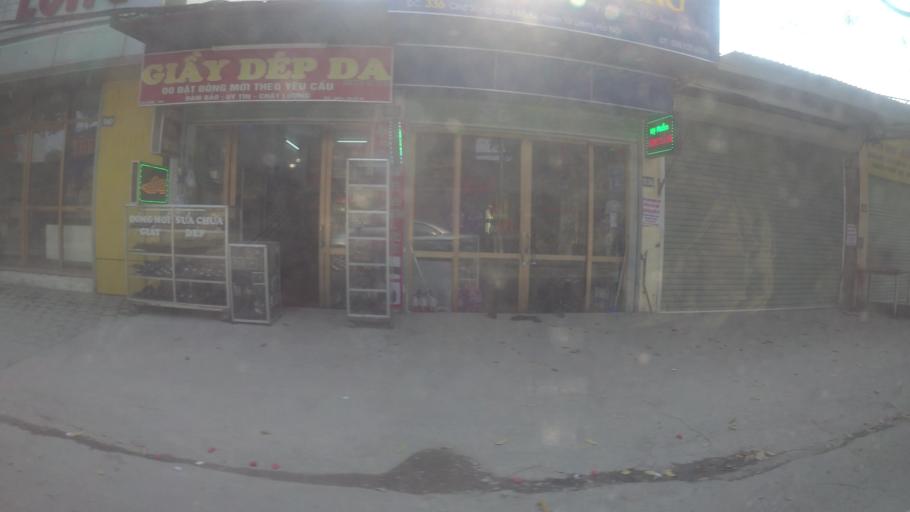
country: VN
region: Ha Noi
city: Ha Dong
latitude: 20.9973
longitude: 105.7521
